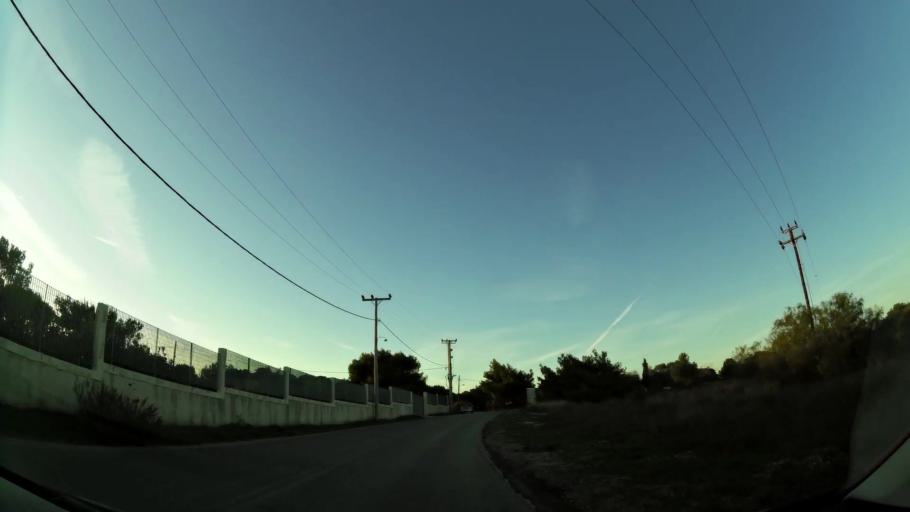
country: GR
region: Attica
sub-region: Nomarchia Anatolikis Attikis
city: Rafina
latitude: 38.0012
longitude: 24.0202
